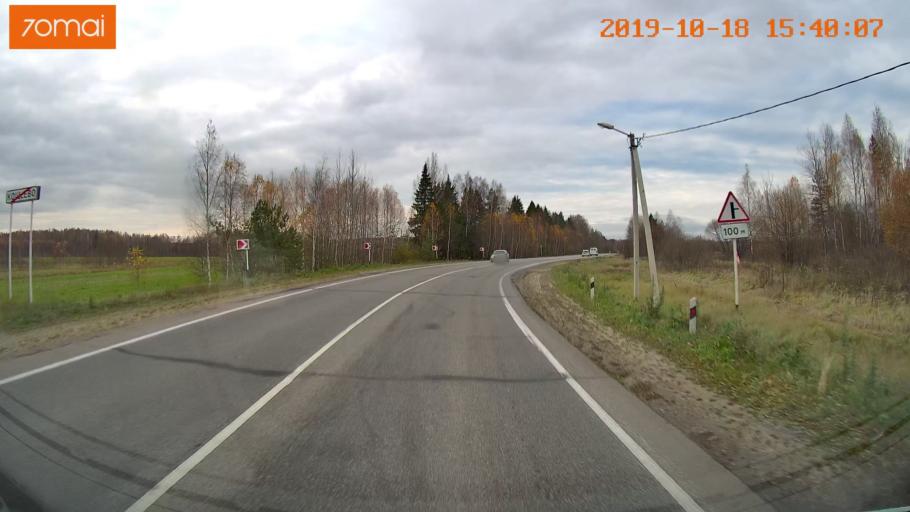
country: RU
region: Vladimir
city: Golovino
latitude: 55.9295
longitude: 40.5957
